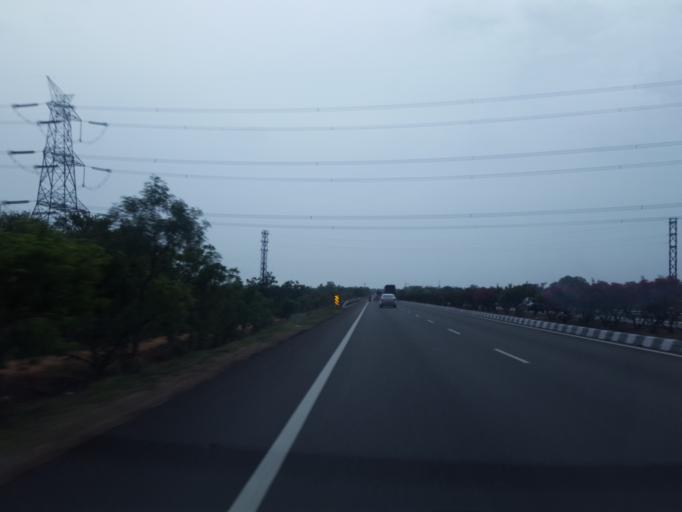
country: IN
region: Telangana
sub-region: Mahbubnagar
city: Farrukhnagar
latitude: 17.0831
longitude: 78.2326
